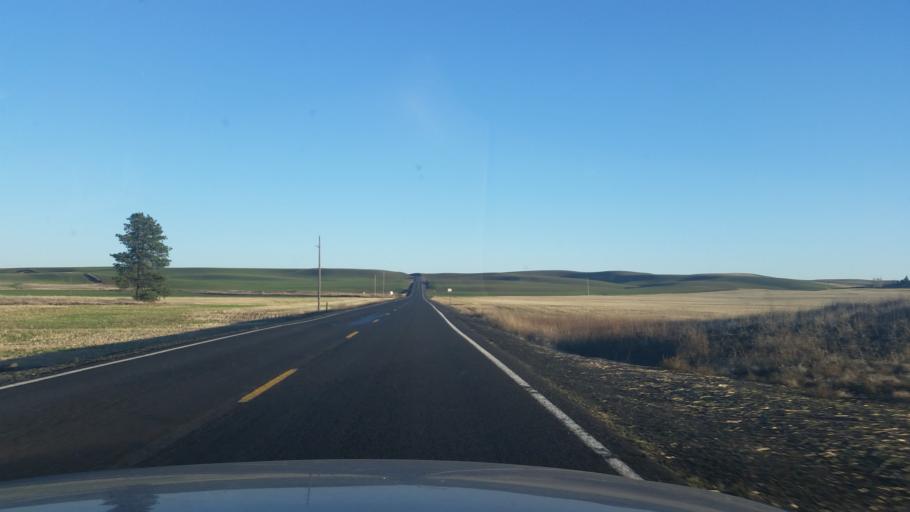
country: US
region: Washington
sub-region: Spokane County
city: Opportunity
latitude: 47.3638
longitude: -117.2852
